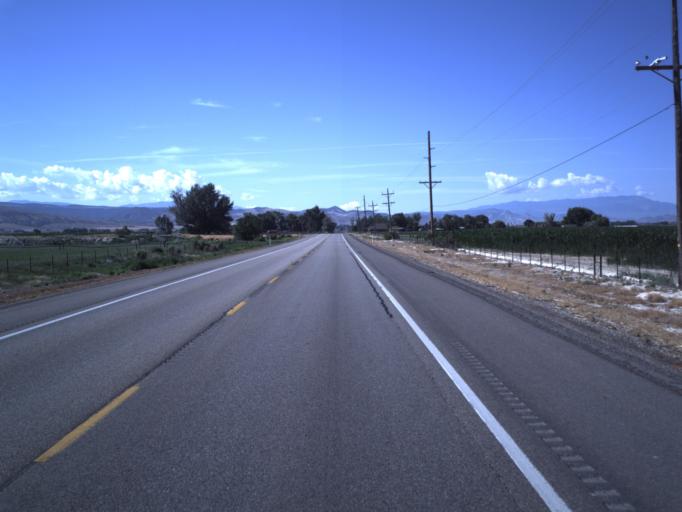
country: US
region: Utah
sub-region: Sanpete County
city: Centerfield
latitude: 39.1038
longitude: -111.8198
